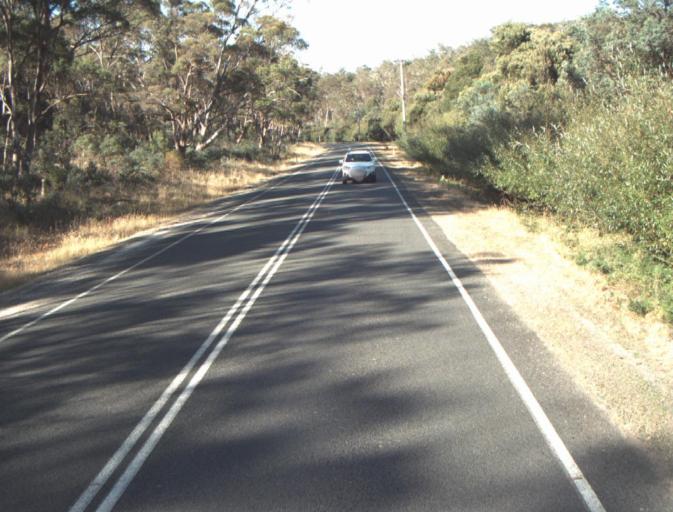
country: AU
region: Tasmania
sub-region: Launceston
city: Newstead
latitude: -41.4185
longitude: 147.2586
